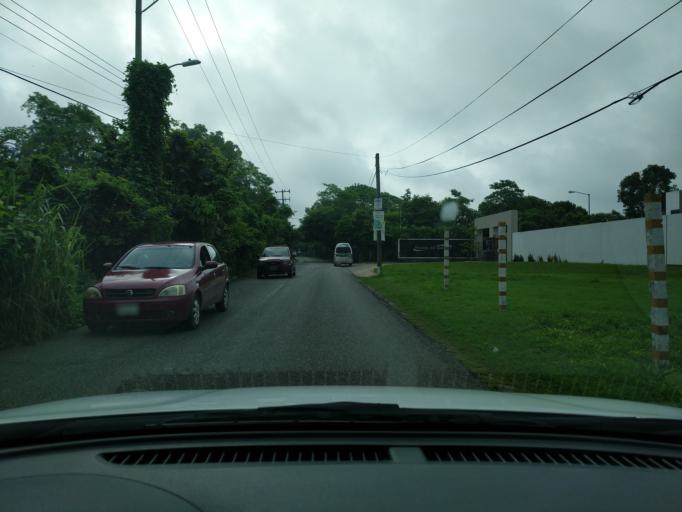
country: MX
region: Tabasco
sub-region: Centro
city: La Lima
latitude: 17.9485
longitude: -92.9638
